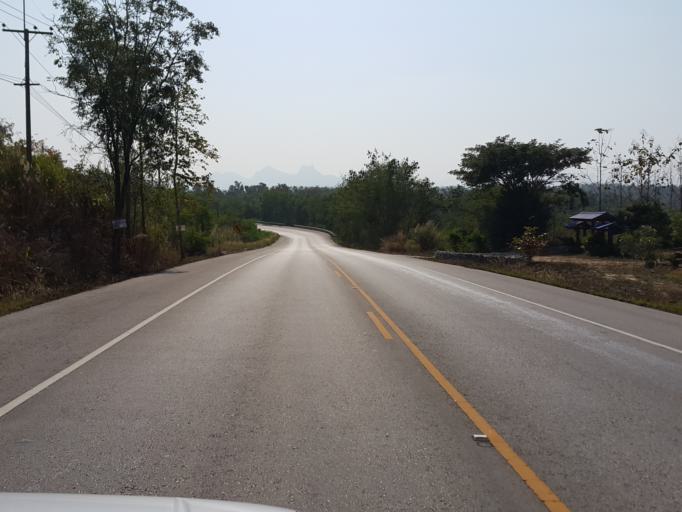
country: TH
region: Lampang
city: Mueang Pan
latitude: 18.8342
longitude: 99.6008
